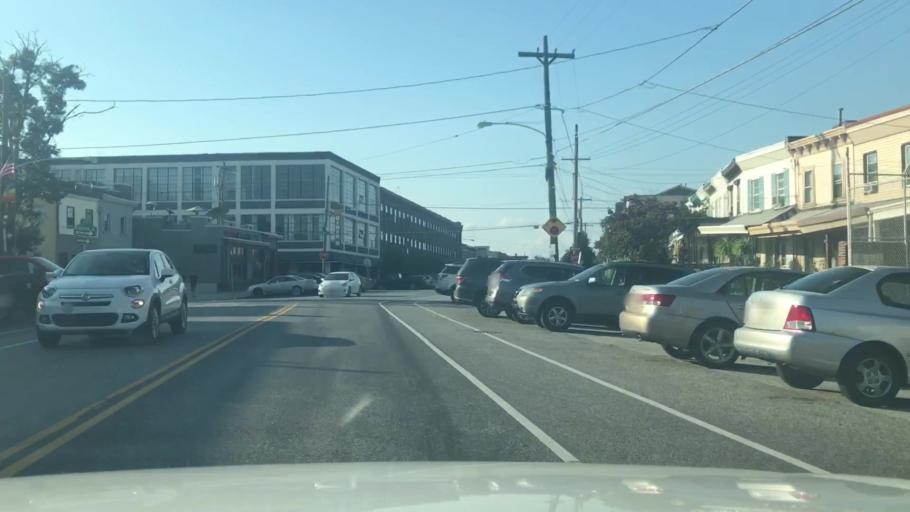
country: US
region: Pennsylvania
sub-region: Philadelphia County
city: Philadelphia
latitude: 39.9767
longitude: -75.1232
